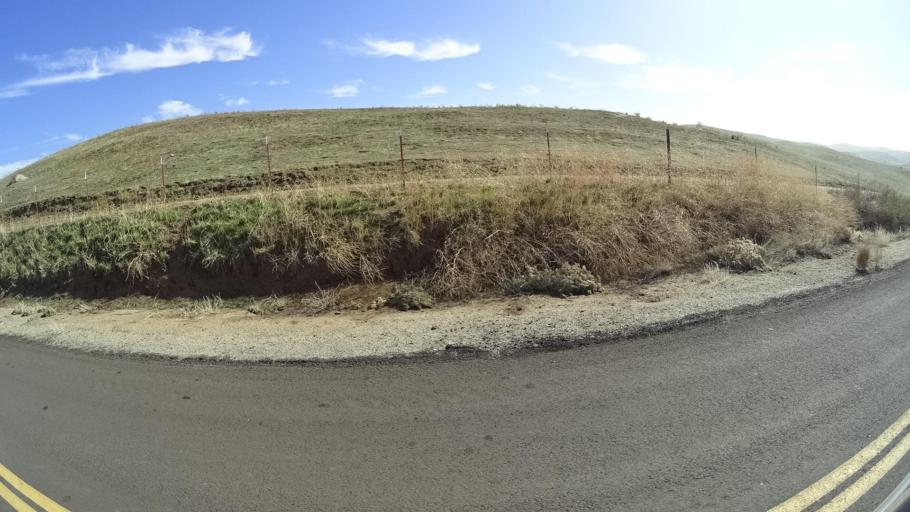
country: US
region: California
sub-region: Tulare County
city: Richgrove
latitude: 35.6827
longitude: -118.8917
